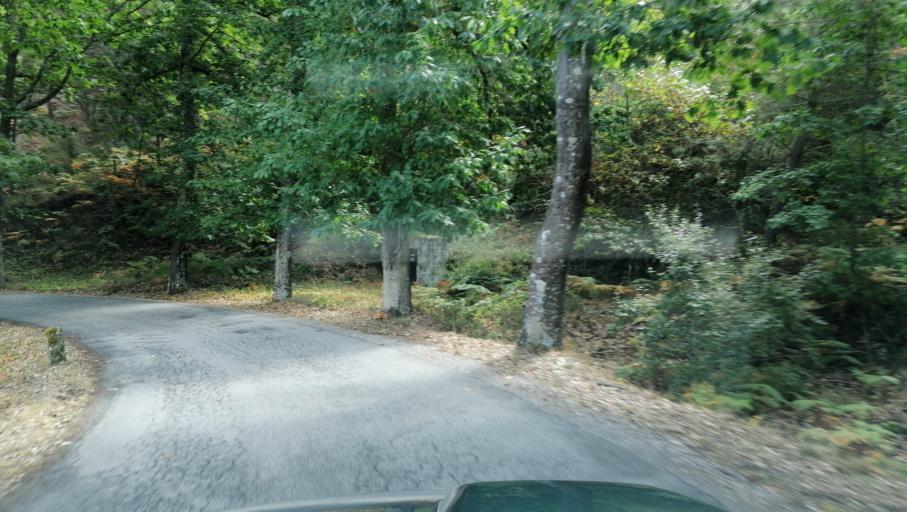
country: PT
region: Vila Real
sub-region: Vila Pouca de Aguiar
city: Vila Pouca de Aguiar
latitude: 41.5314
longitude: -7.5967
